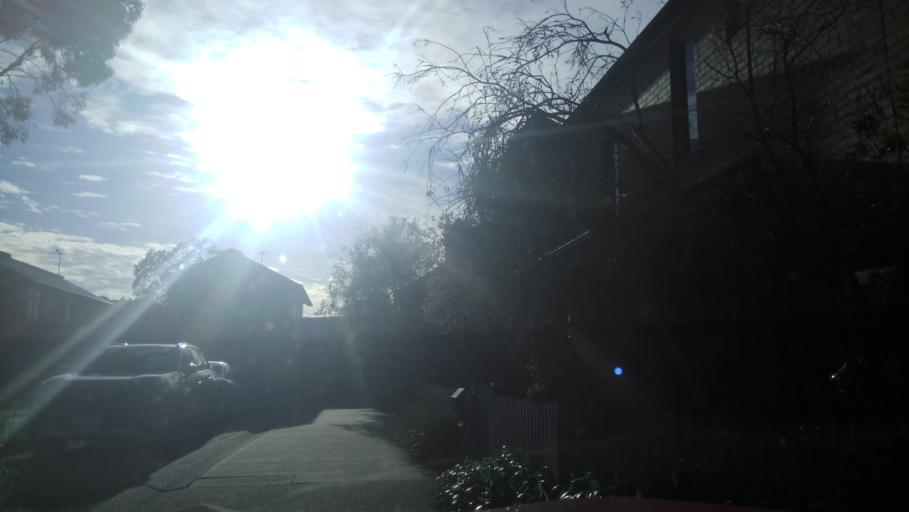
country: AU
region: Victoria
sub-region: Hobsons Bay
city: Williamstown North
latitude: -37.8585
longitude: 144.8827
